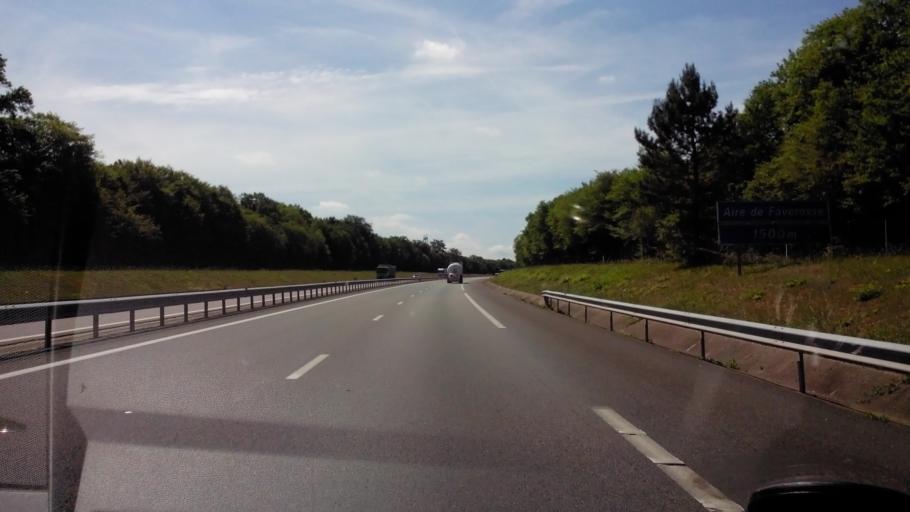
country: FR
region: Lorraine
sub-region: Departement de Meurthe-et-Moselle
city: Colombey-les-Belles
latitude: 48.5260
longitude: 5.9142
